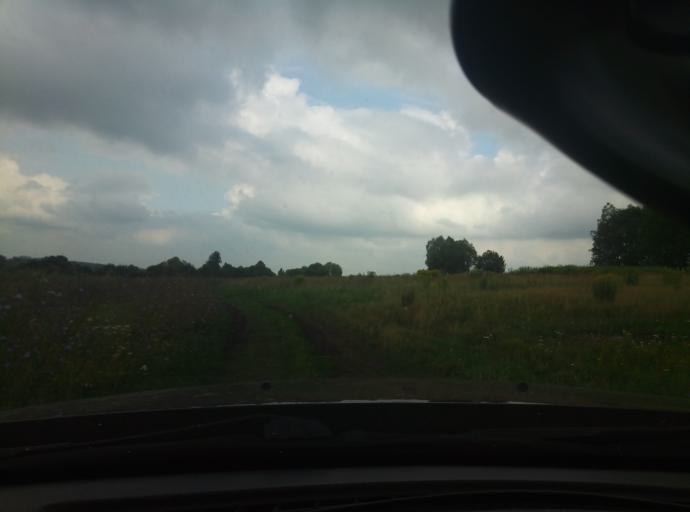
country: RU
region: Tula
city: Shvartsevskiy
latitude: 54.0801
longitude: 38.0217
